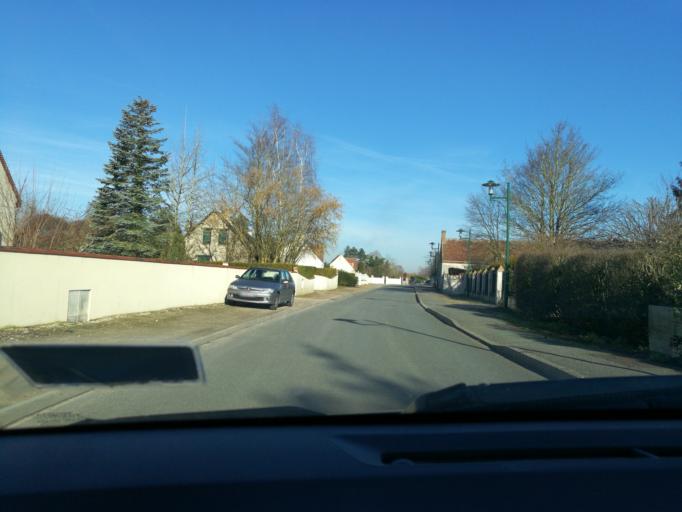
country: FR
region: Centre
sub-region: Departement du Loiret
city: Chaingy
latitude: 47.8776
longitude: 1.7664
